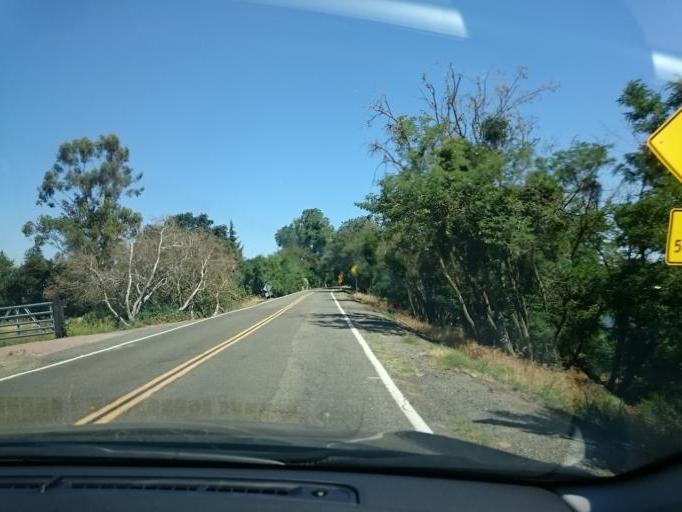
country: US
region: California
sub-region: Sacramento County
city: Parkway
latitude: 38.4562
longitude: -121.5035
